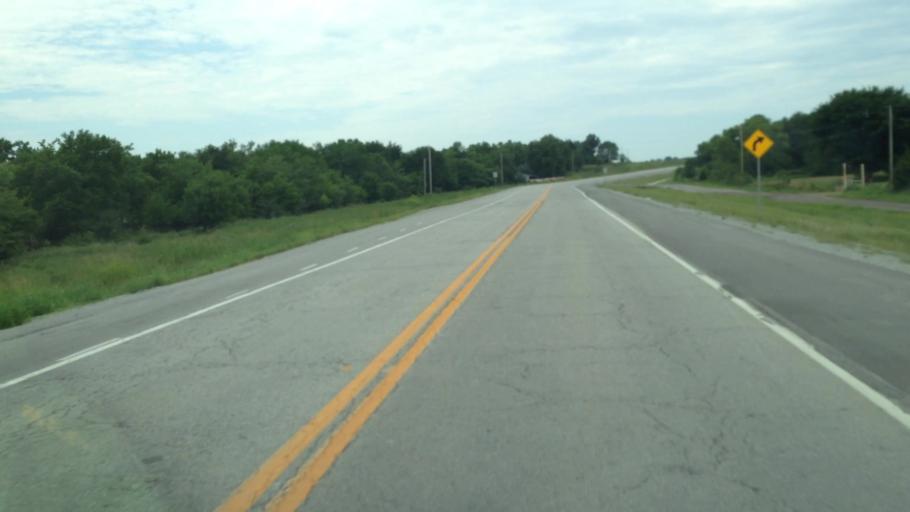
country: US
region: Kansas
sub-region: Labette County
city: Chetopa
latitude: 36.8837
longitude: -95.0989
